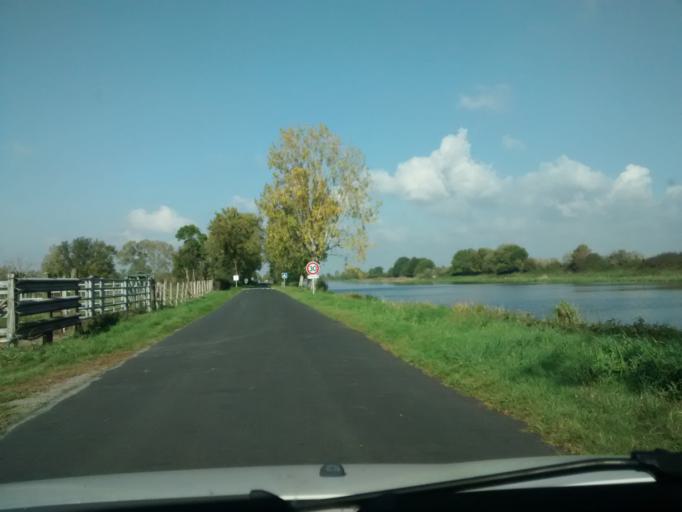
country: FR
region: Pays de la Loire
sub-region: Departement de la Loire-Atlantique
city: Frossay
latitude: 47.2545
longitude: -1.9071
